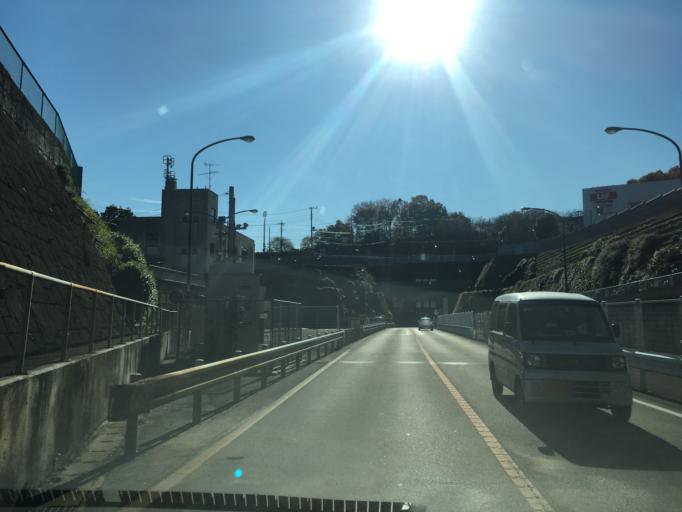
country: JP
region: Tokyo
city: Hachioji
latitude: 35.6787
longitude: 139.3404
